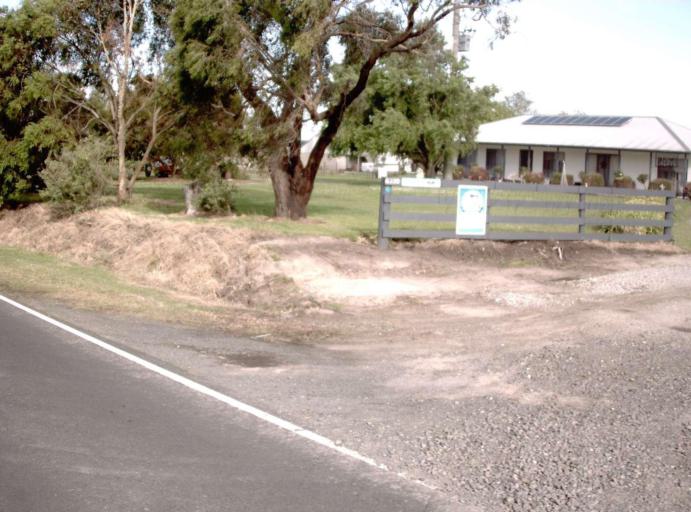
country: AU
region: Victoria
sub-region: Bass Coast
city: North Wonthaggi
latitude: -38.6157
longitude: 145.7434
